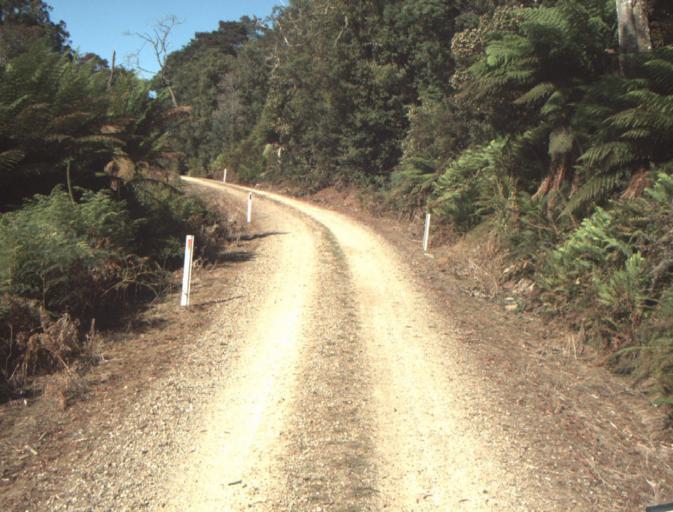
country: AU
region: Tasmania
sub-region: Dorset
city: Scottsdale
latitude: -41.2737
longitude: 147.3634
